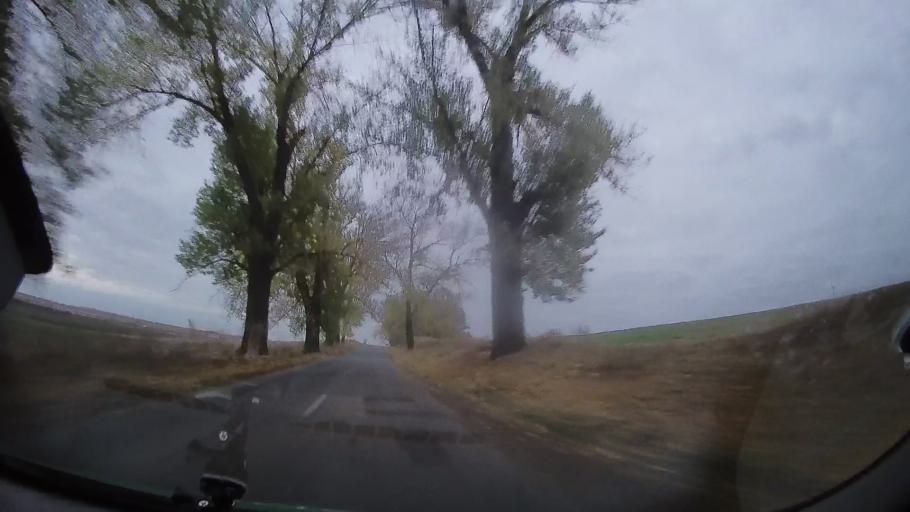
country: RO
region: Tulcea
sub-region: Comuna Mihai Bravu
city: Turda
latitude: 44.9665
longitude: 28.6327
